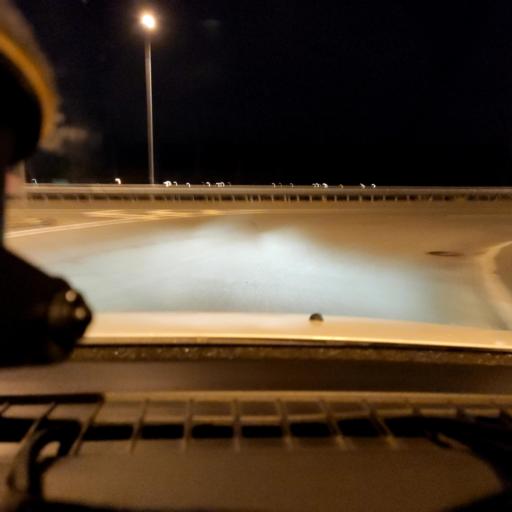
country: RU
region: Samara
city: Bereza
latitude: 53.5140
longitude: 50.1517
